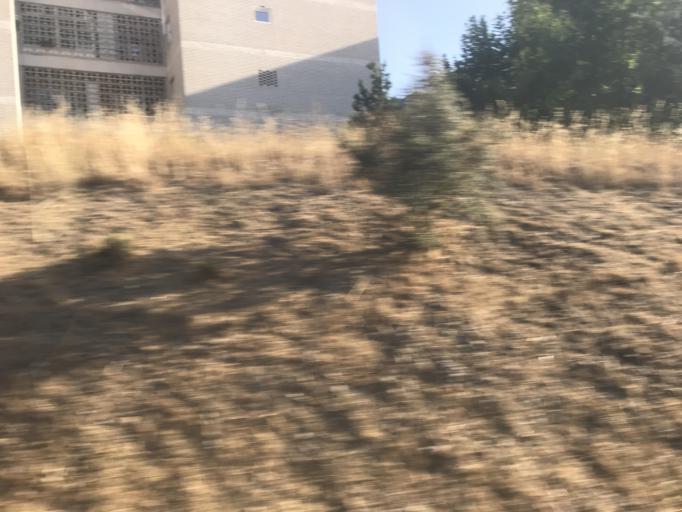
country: ES
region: Madrid
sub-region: Provincia de Madrid
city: Majadahonda
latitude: 40.4735
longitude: -3.8426
